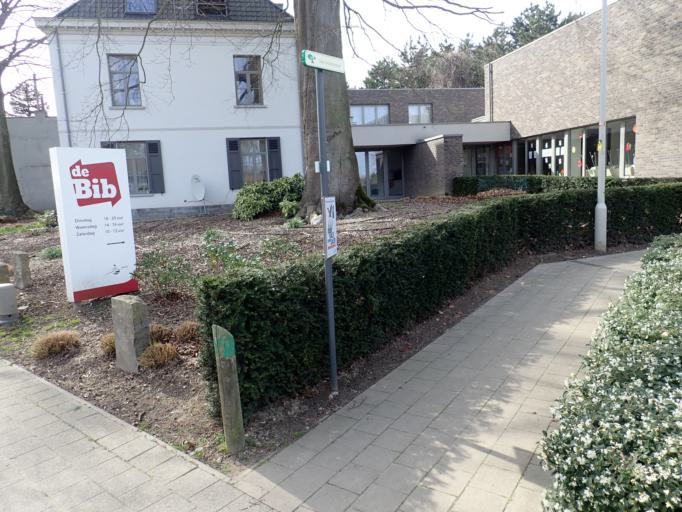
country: BE
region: Flanders
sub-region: Provincie Antwerpen
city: Lier
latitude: 51.1635
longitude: 4.6071
